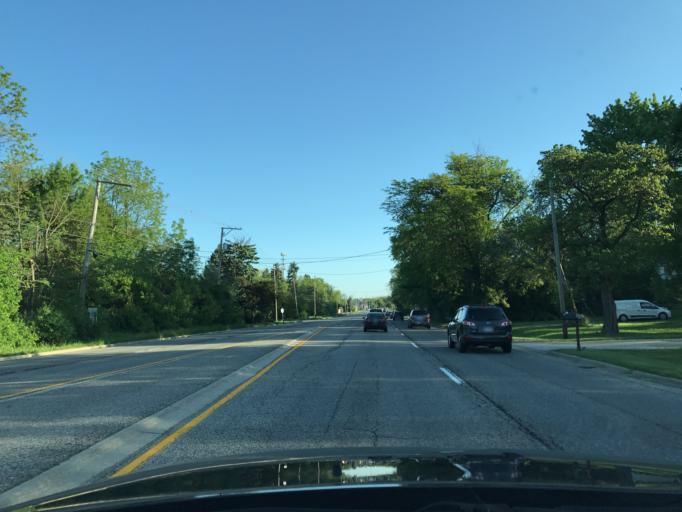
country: US
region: Illinois
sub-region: DuPage County
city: Lisle
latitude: 41.7810
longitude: -88.0727
